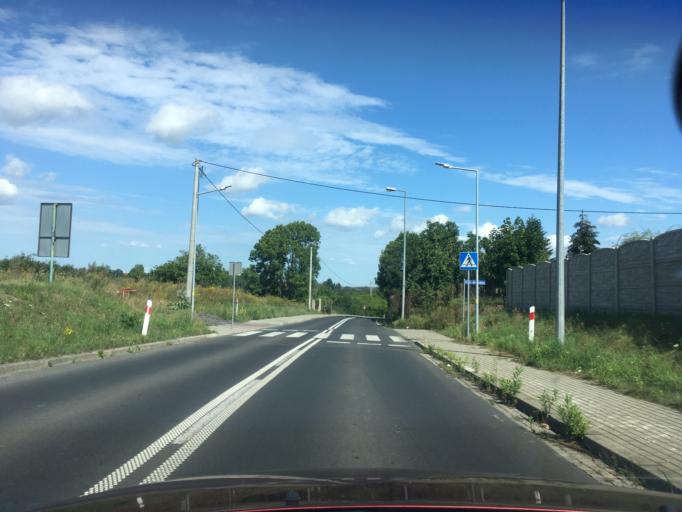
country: DE
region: Saxony
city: Goerlitz
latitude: 51.1611
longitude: 14.9980
